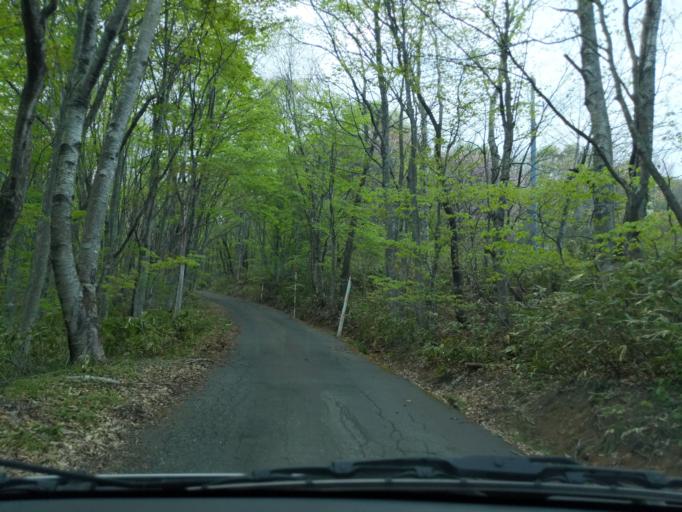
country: JP
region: Iwate
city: Ichinoseki
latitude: 38.9259
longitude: 140.8242
